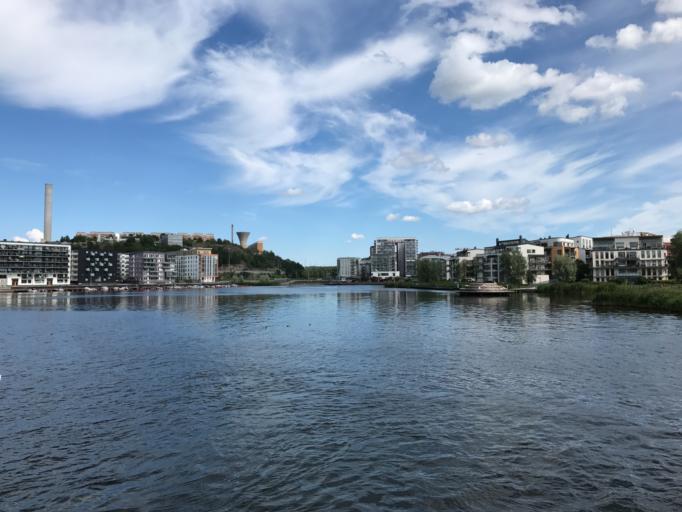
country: SE
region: Stockholm
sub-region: Stockholms Kommun
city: OEstermalm
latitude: 59.3062
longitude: 18.0990
